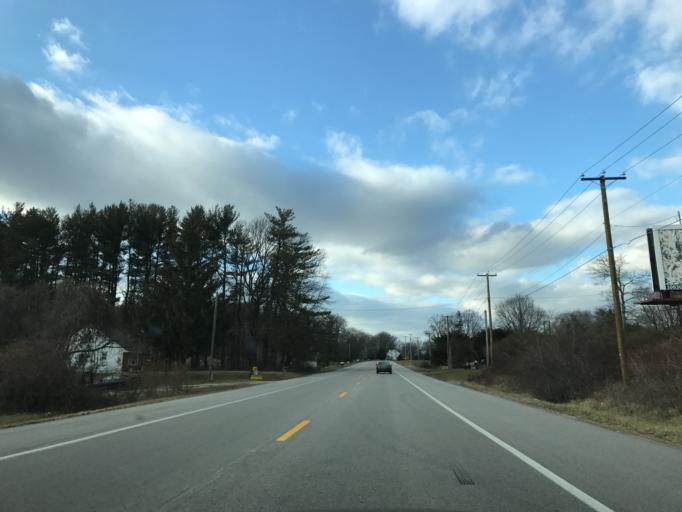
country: US
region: Maryland
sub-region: Cecil County
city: North East
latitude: 39.6508
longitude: -75.9726
